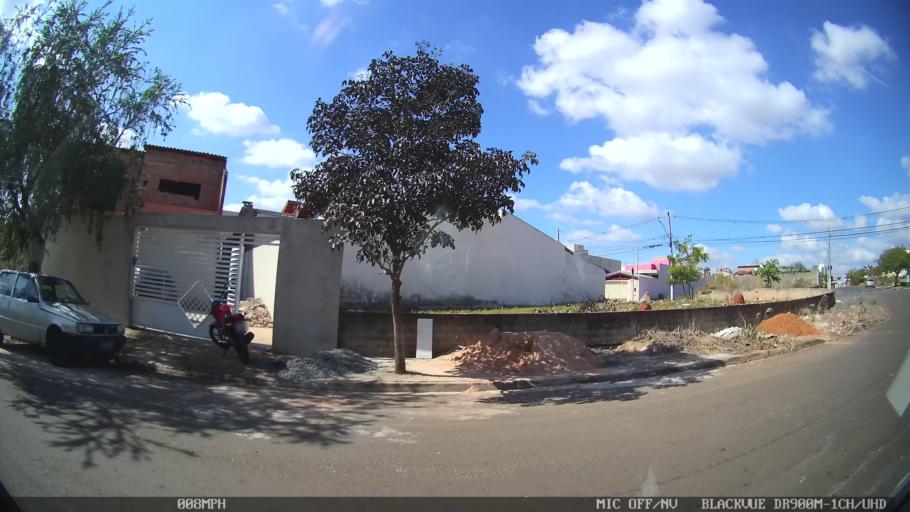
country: BR
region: Sao Paulo
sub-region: Hortolandia
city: Hortolandia
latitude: -22.8832
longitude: -47.2217
